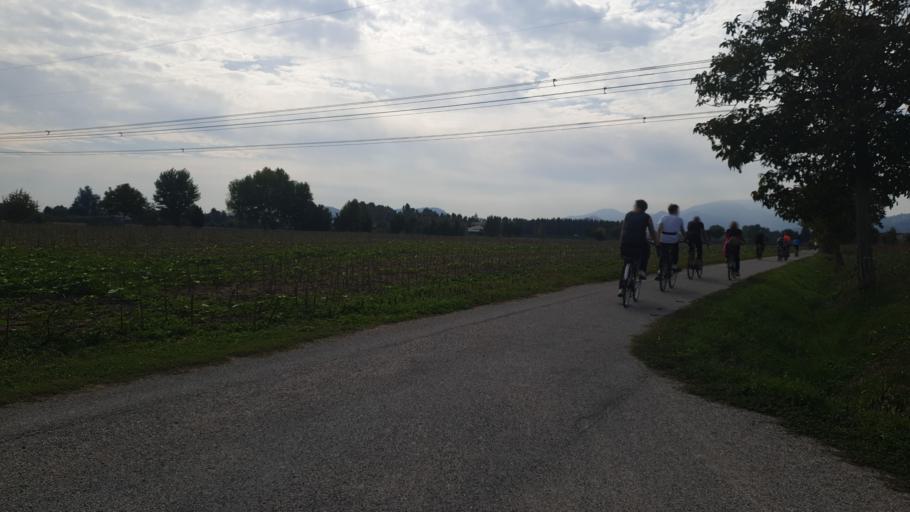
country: IT
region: Veneto
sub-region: Provincia di Padova
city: Cervarese Santa Croce
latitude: 45.4089
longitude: 11.6967
